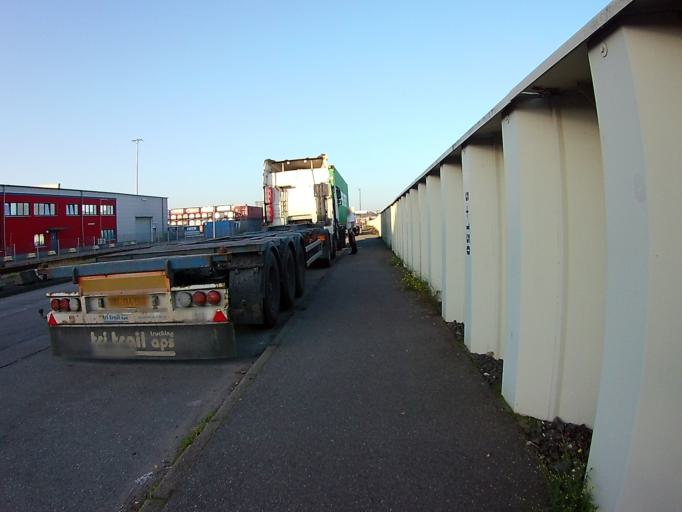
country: DE
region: Hamburg
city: Altona
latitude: 53.5284
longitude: 9.9364
